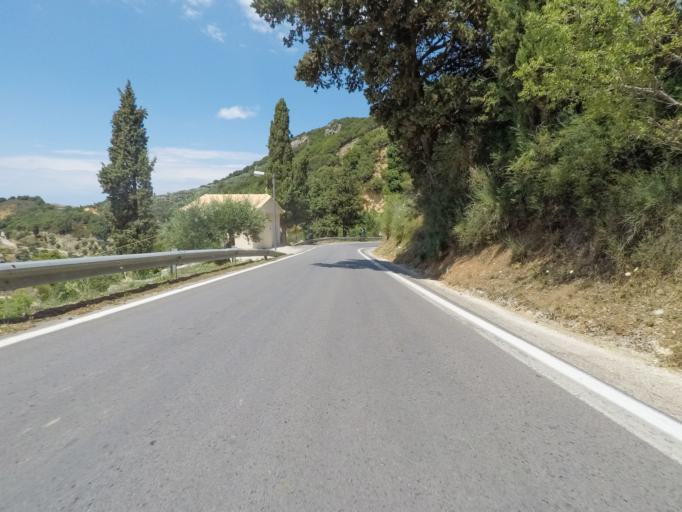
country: GR
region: Crete
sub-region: Nomos Irakleiou
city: Mokhos
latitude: 35.2241
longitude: 25.4623
